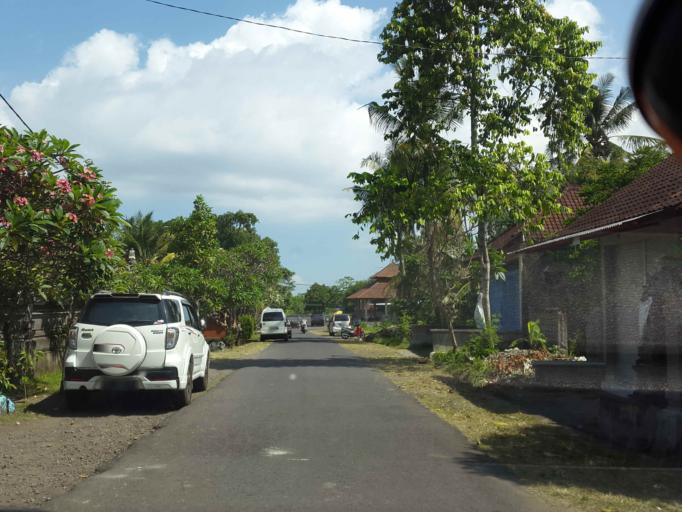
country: ID
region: Bali
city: Klungkung
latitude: -8.5507
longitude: 115.3738
